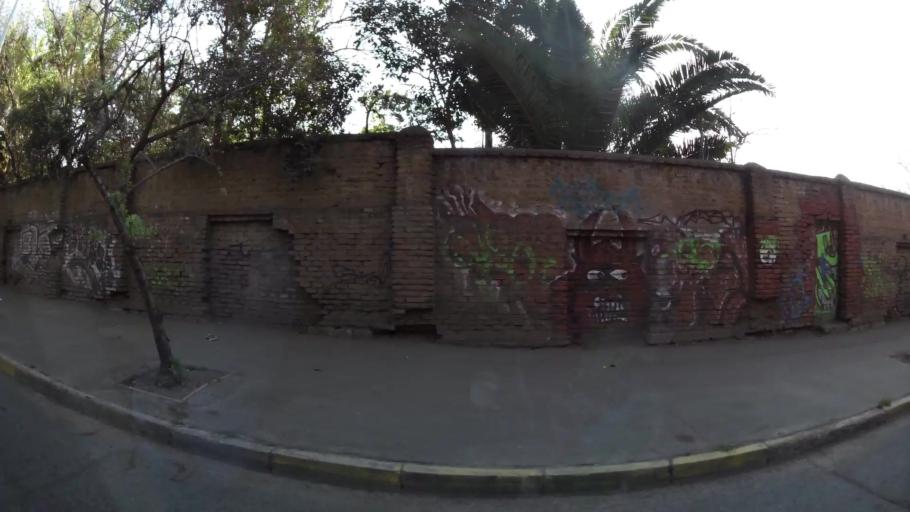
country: CL
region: Santiago Metropolitan
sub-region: Provincia de Santiago
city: Santiago
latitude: -33.4198
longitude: -70.6488
